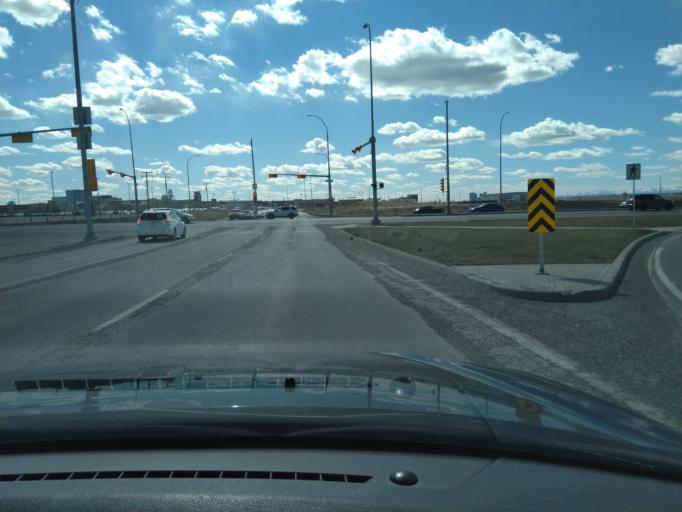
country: CA
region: Alberta
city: Calgary
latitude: 51.1401
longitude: -114.0135
